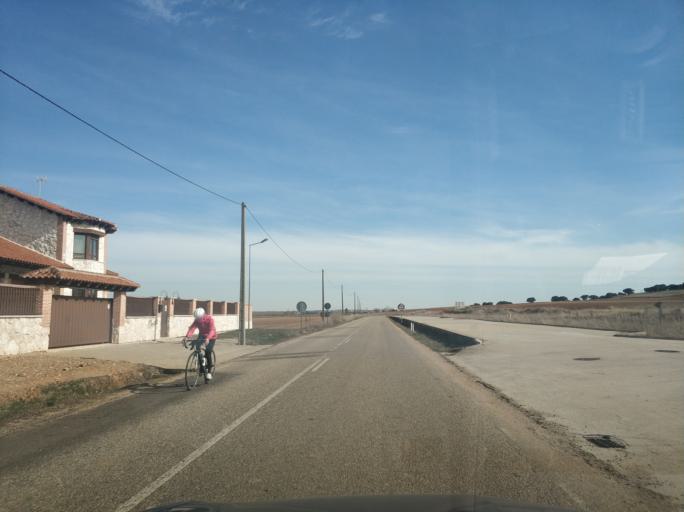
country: ES
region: Castille and Leon
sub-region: Provincia de Salamanca
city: Florida de Liebana
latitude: 41.0256
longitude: -5.7590
